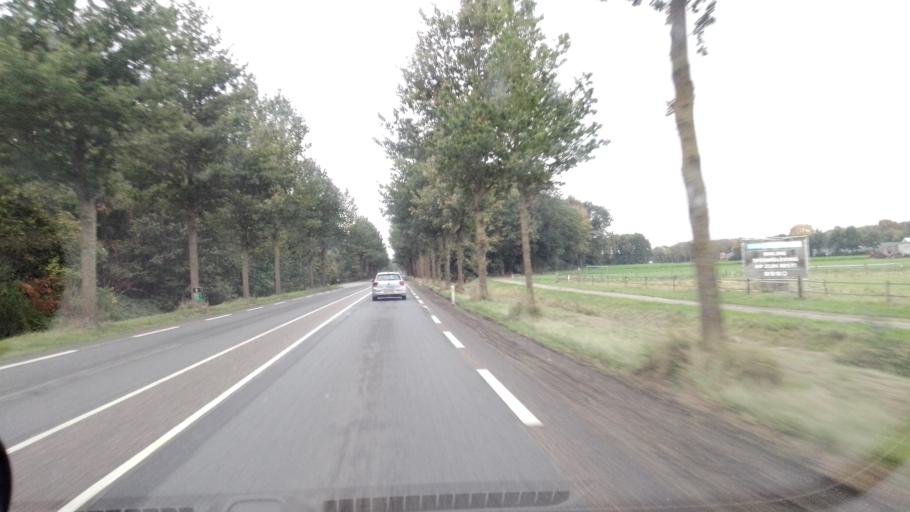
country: NL
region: Limburg
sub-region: Gemeente Venlo
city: Tegelen
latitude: 51.3566
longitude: 6.1191
